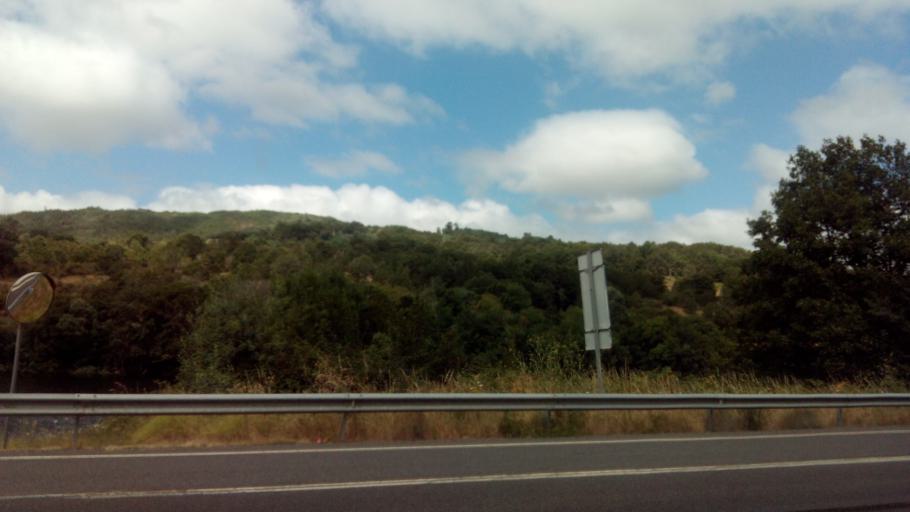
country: ES
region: Galicia
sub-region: Provincia de Ourense
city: Coles
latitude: 42.3959
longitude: -7.7997
